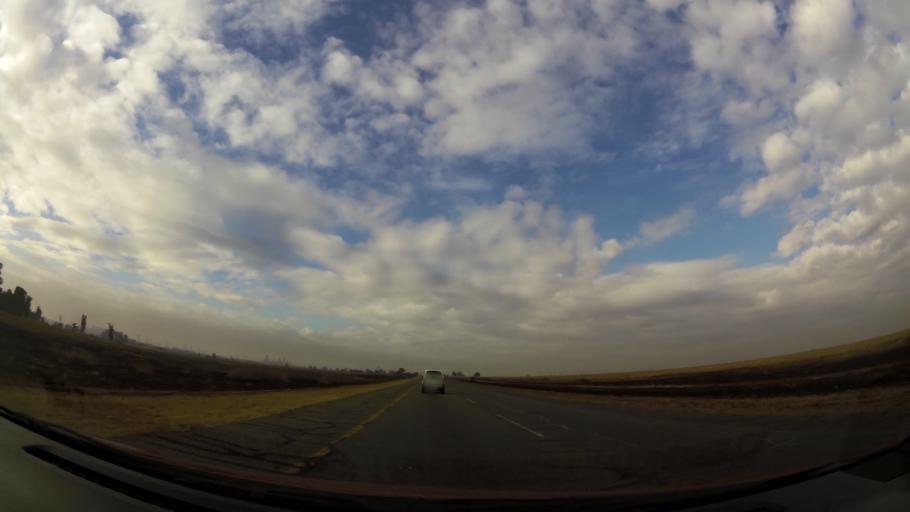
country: ZA
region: Gauteng
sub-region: Sedibeng District Municipality
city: Vanderbijlpark
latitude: -26.6558
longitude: 27.7827
